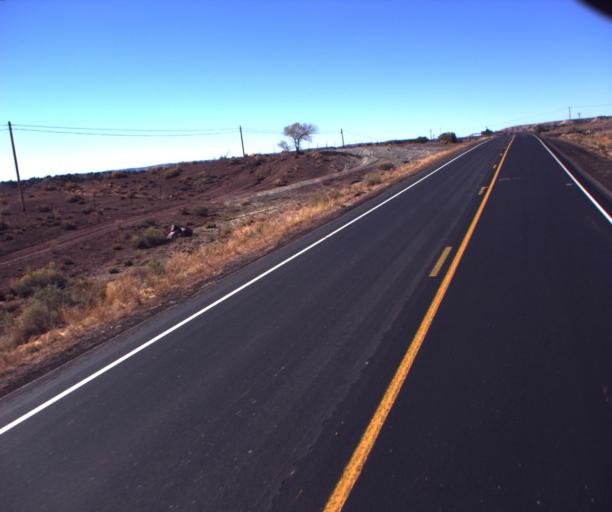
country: US
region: Arizona
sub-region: Apache County
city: Ganado
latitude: 35.7137
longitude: -109.5601
